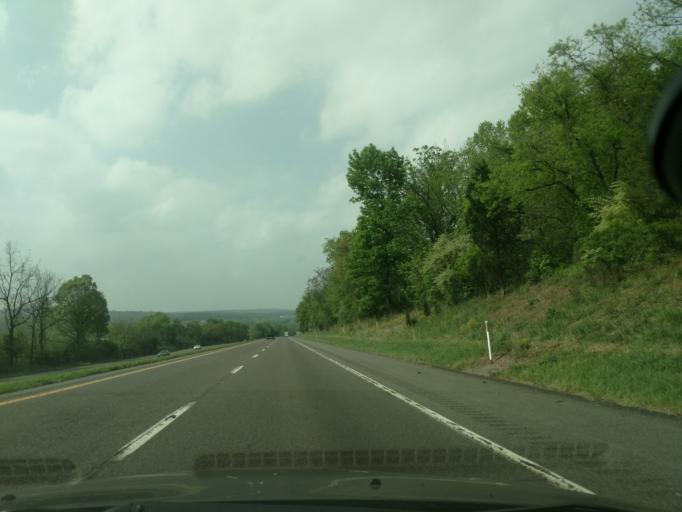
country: US
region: Pennsylvania
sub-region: Berks County
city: Flying Hills
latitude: 40.2317
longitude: -75.9139
